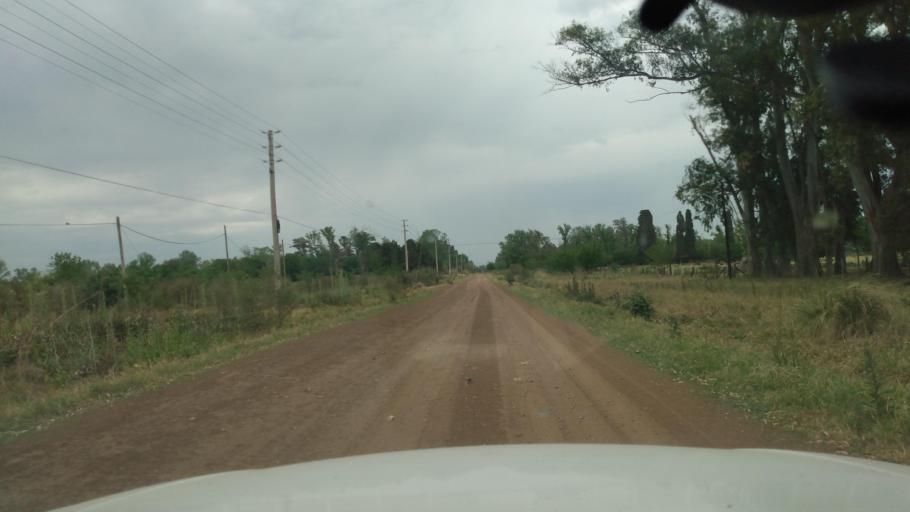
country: AR
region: Buenos Aires
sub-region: Partido de Lujan
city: Lujan
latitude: -34.5546
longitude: -59.1763
